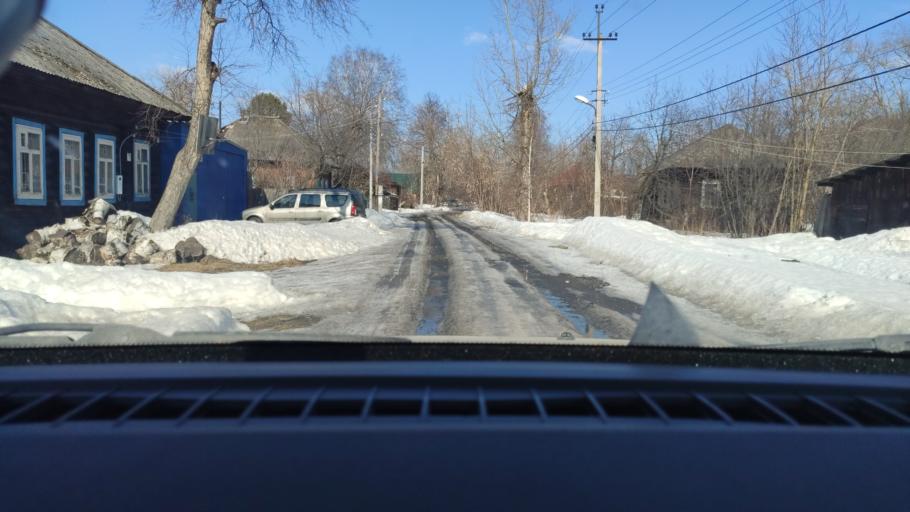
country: RU
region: Perm
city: Perm
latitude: 58.0651
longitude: 56.3400
